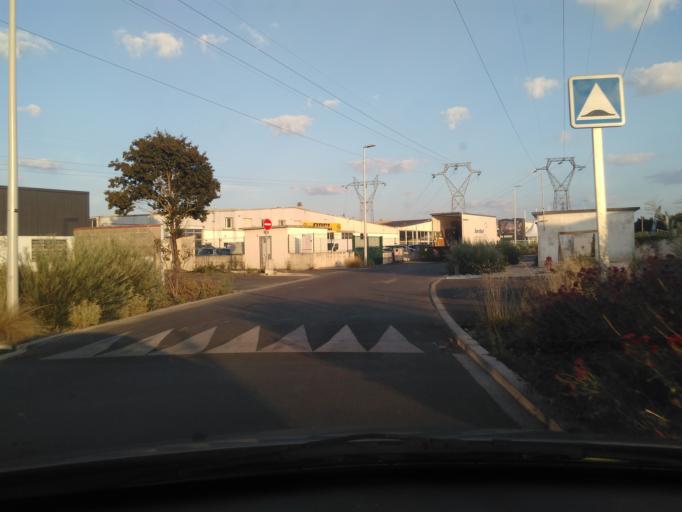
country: FR
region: Poitou-Charentes
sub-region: Departement de la Charente-Maritime
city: Puilboreau
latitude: 46.1770
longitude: -1.1121
